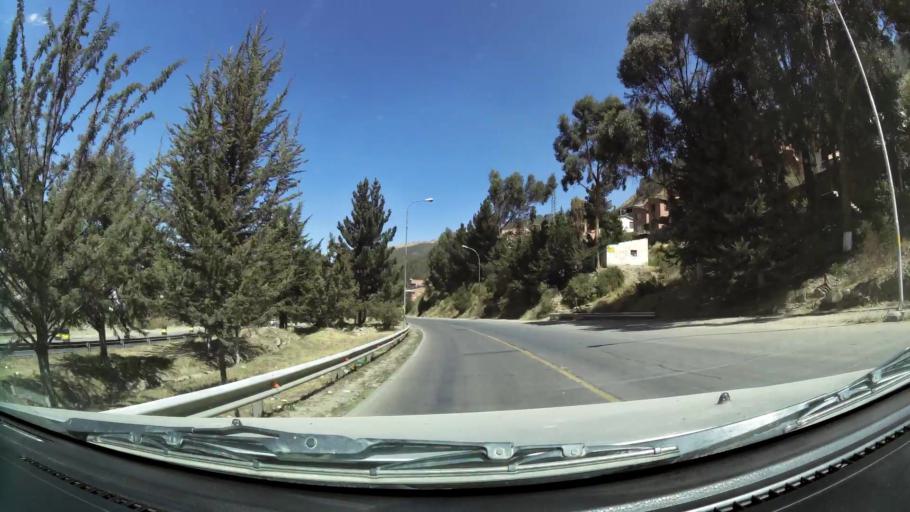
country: BO
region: La Paz
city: La Paz
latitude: -16.4640
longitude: -68.1519
